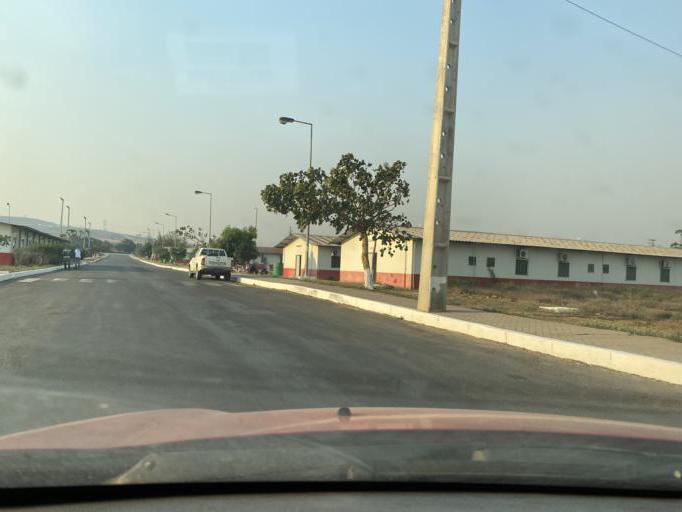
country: AO
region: Cuanza Norte
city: N'dalatando
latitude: -9.7429
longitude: 15.1407
